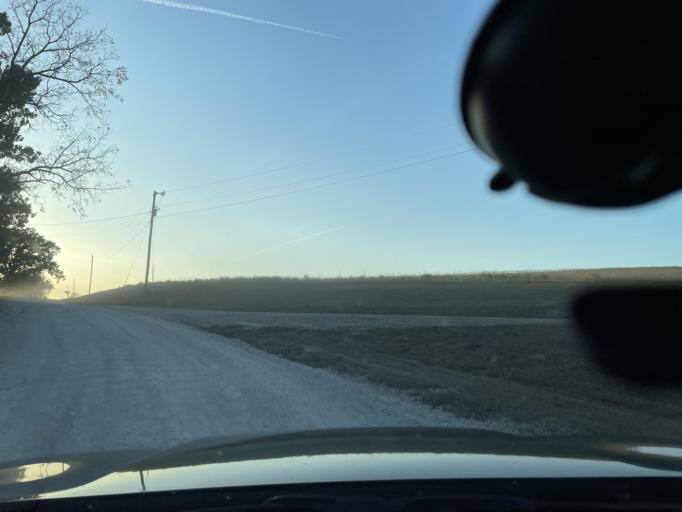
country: US
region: Missouri
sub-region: Andrew County
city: Savannah
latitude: 39.9302
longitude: -94.8613
